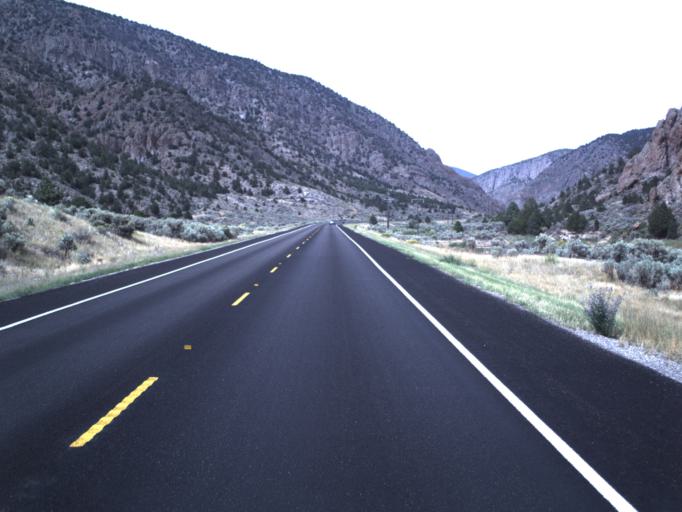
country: US
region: Utah
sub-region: Piute County
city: Junction
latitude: 38.0809
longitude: -112.3400
